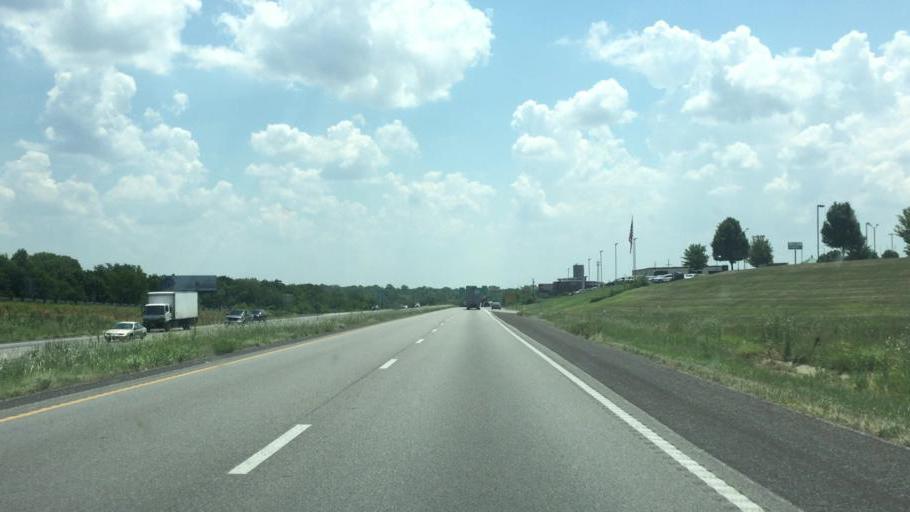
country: US
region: Missouri
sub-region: Platte County
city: Platte City
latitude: 39.3525
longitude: -94.7609
